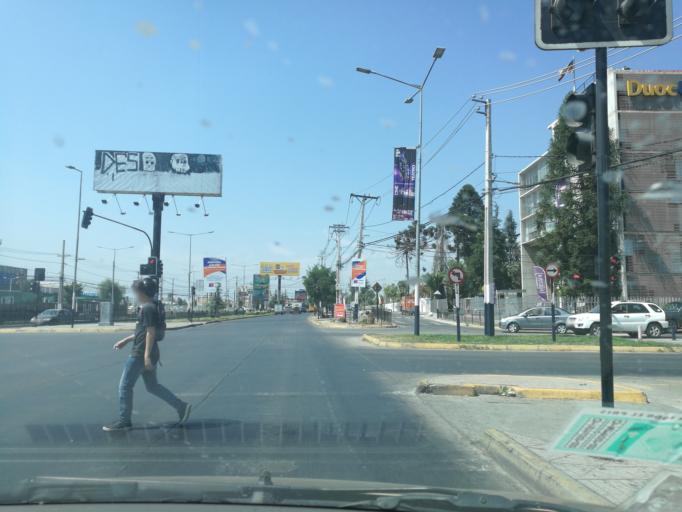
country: CL
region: Santiago Metropolitan
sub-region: Provincia de Cordillera
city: Puente Alto
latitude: -33.5978
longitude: -70.5783
